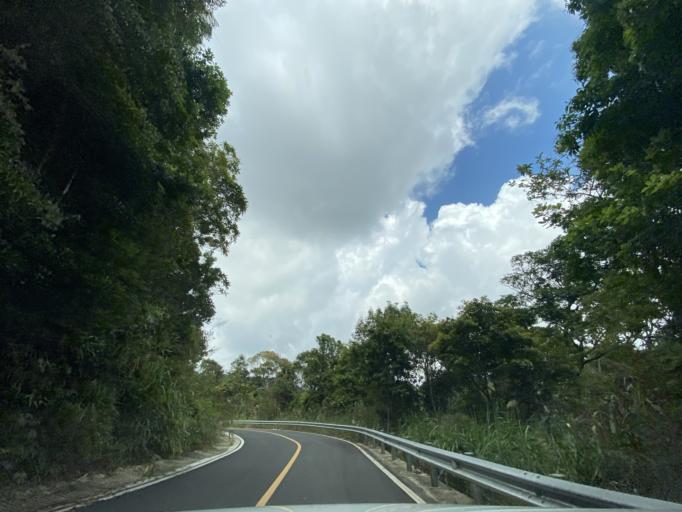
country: CN
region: Hainan
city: Diaoluoshan
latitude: 18.7092
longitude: 109.8830
